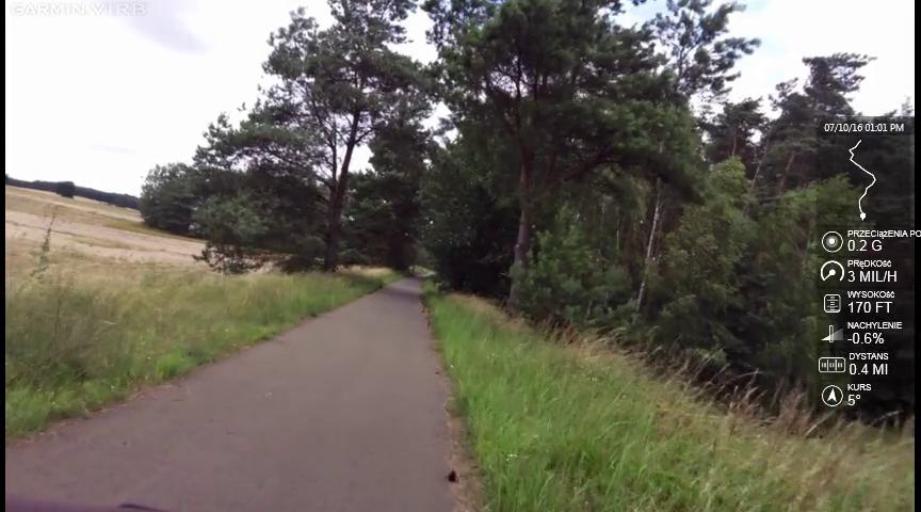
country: PL
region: West Pomeranian Voivodeship
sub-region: Powiat gryfinski
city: Banie
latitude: 53.0435
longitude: 14.6325
